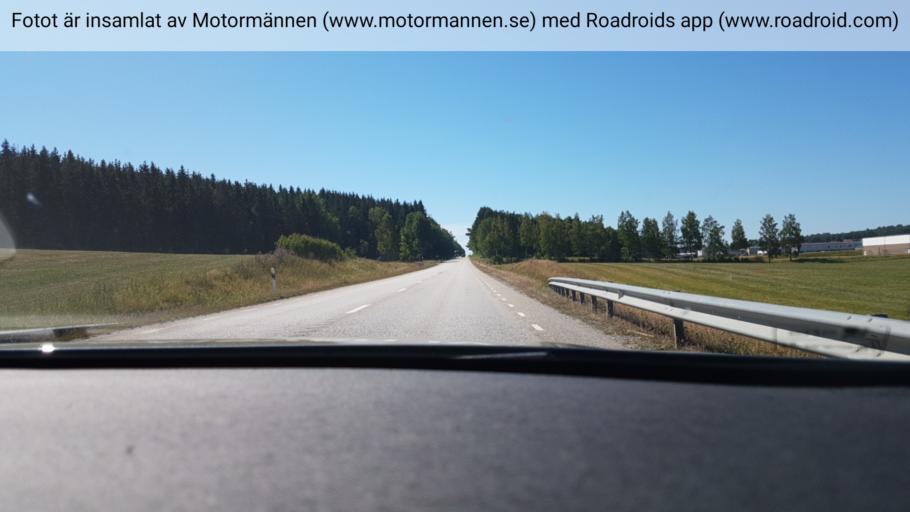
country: SE
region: Joenkoeping
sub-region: Habo Kommun
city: Habo
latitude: 57.9096
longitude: 14.1034
